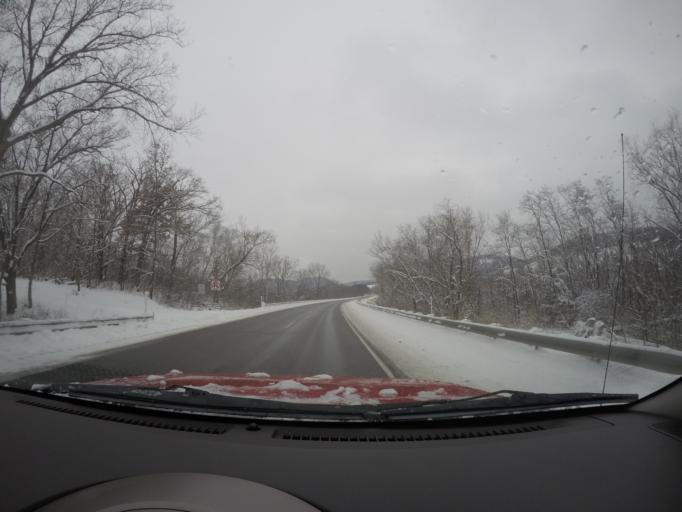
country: US
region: Wisconsin
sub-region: La Crosse County
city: Brice Prairie
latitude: 43.9169
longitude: -91.3674
